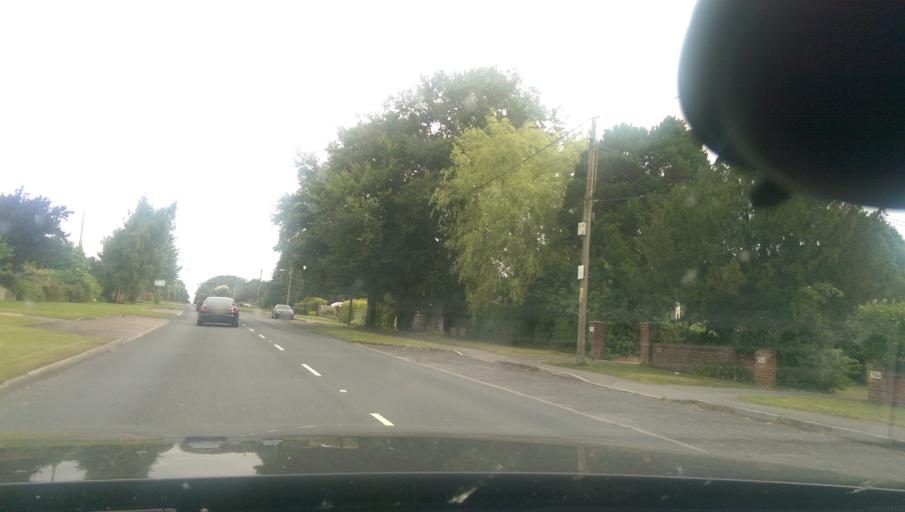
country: GB
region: England
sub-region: Wiltshire
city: Amesbury
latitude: 51.1829
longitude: -1.7830
